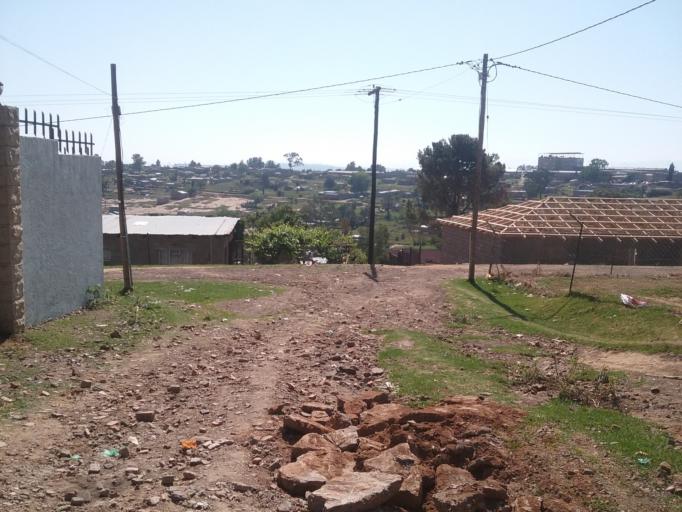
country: LS
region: Berea
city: Teyateyaneng
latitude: -29.1480
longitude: 27.7426
